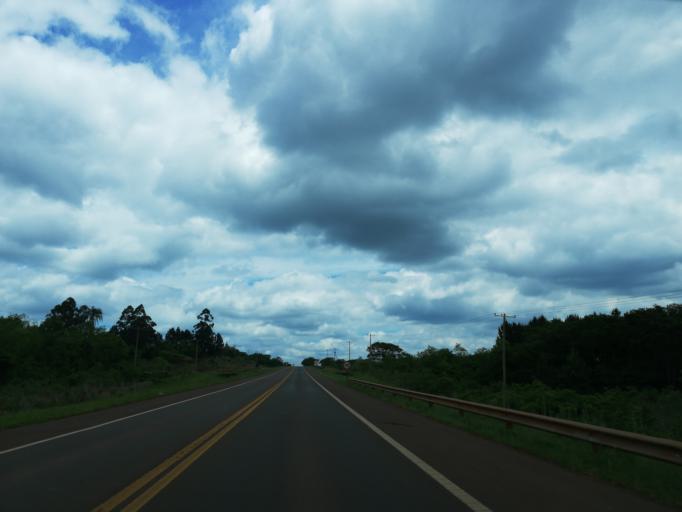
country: AR
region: Misiones
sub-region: Departamento de Leandro N. Alem
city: Leandro N. Alem
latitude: -27.6300
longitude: -55.3408
